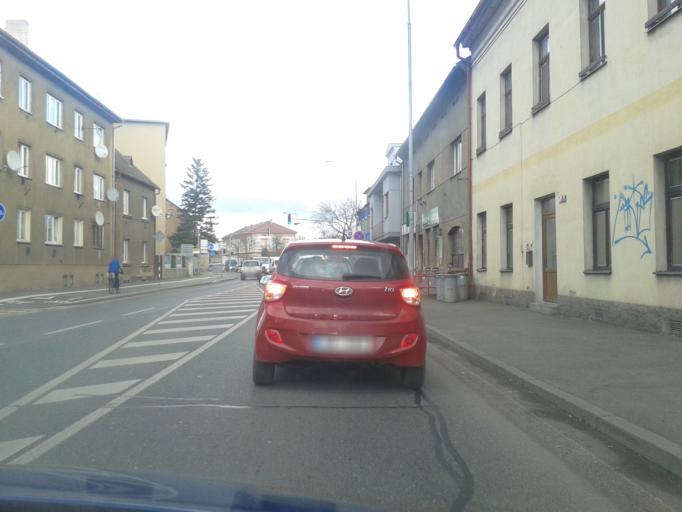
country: CZ
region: Central Bohemia
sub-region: Okres Beroun
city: Beroun
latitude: 49.9592
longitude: 14.0626
